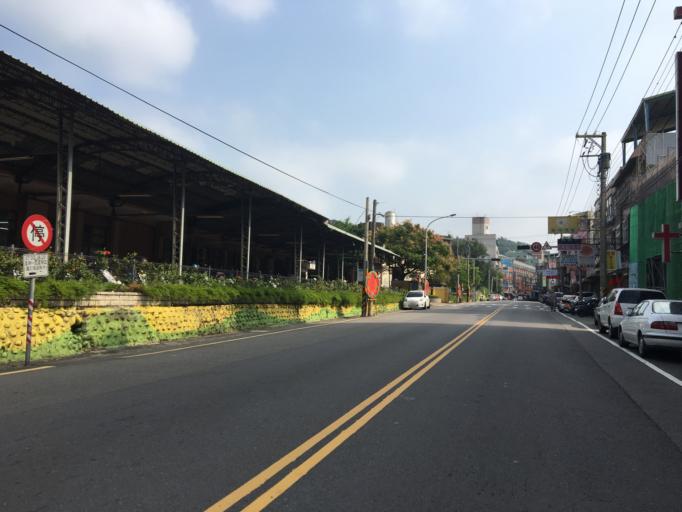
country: TW
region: Taiwan
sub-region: Hsinchu
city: Hsinchu
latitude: 24.7905
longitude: 120.9650
